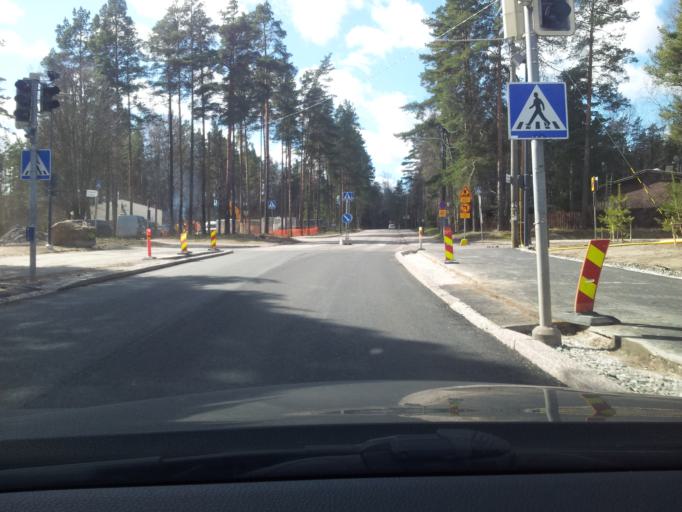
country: FI
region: Uusimaa
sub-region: Helsinki
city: Kauniainen
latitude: 60.1523
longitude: 24.6951
